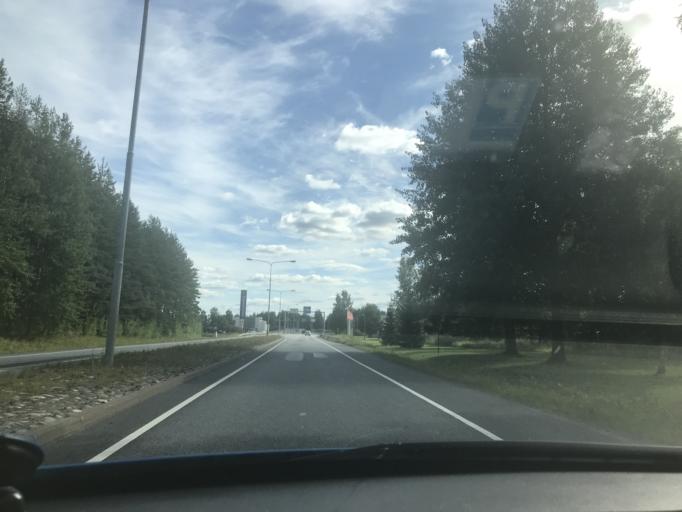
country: FI
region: Southern Ostrobothnia
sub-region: Kuusiokunnat
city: Alavus
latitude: 62.5907
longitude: 23.6131
